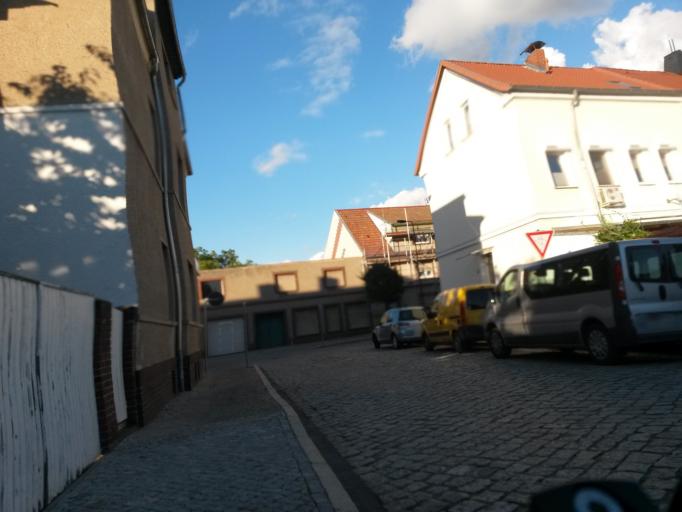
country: DE
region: Saxony-Anhalt
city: Tangermunde
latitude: 52.5467
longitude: 11.9746
